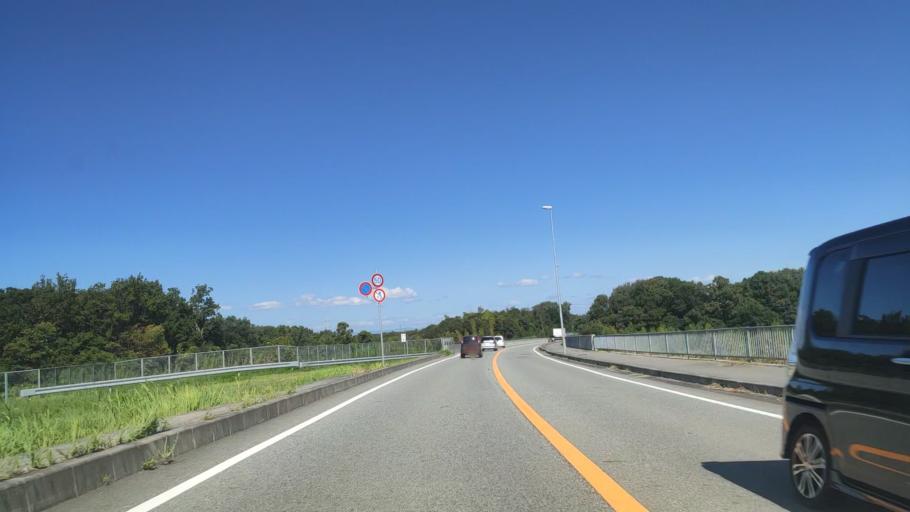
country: JP
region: Hyogo
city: Miki
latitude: 34.7561
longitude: 134.9768
